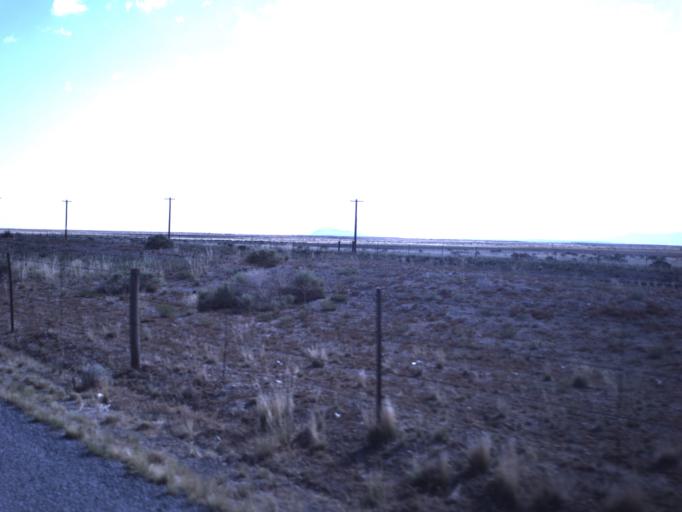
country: US
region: Utah
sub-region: Millard County
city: Delta
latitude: 38.9310
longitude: -112.8098
